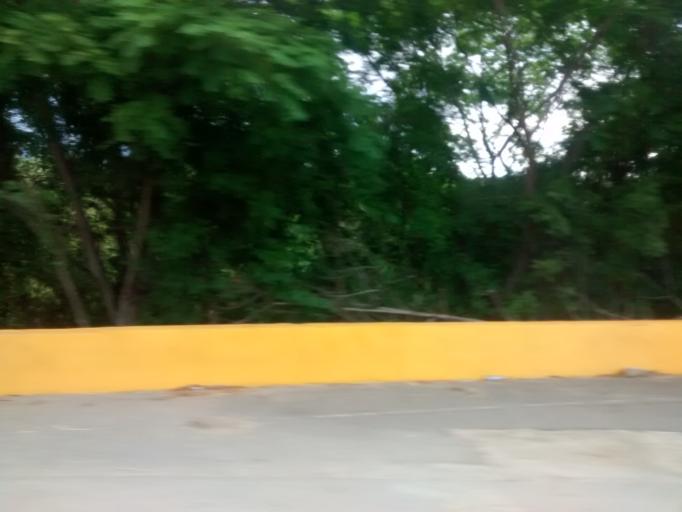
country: CO
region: Cundinamarca
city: Ricaurte
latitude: 4.2361
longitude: -74.7134
